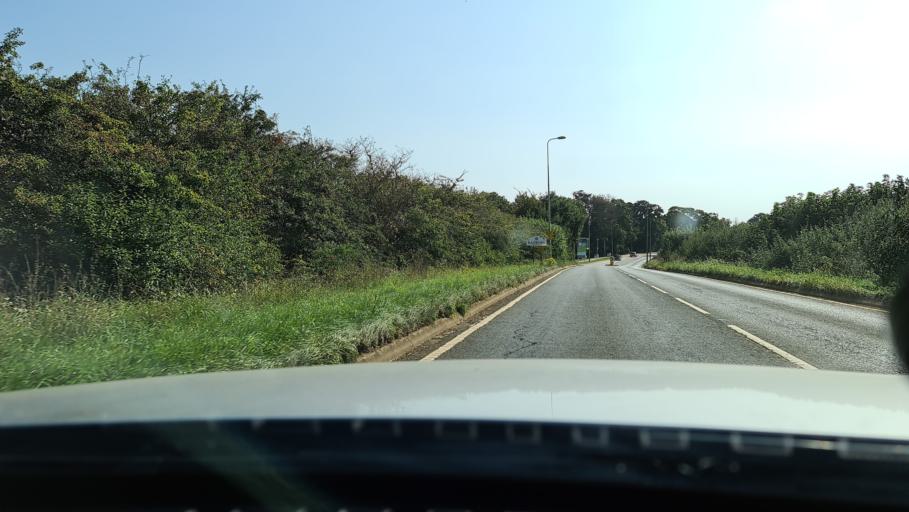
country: GB
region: England
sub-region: Oxfordshire
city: Hanwell
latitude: 52.0819
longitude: -1.3700
